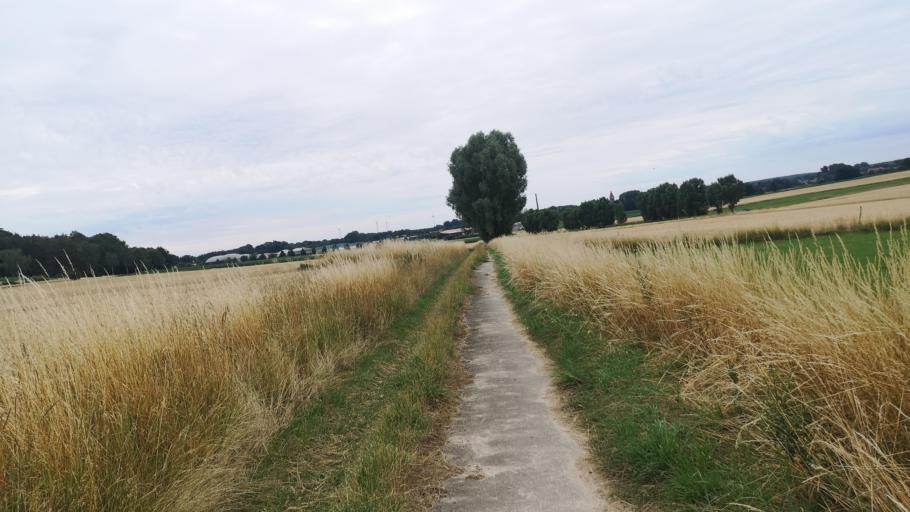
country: DE
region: Lower Saxony
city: Dahlem
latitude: 53.2007
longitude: 10.7489
